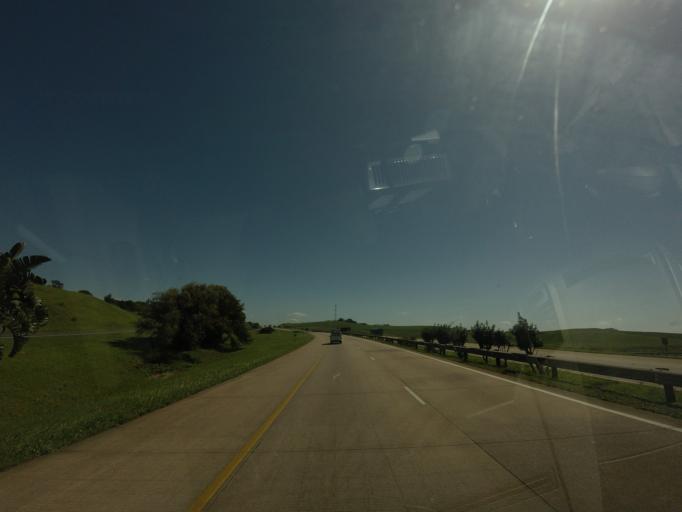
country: ZA
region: KwaZulu-Natal
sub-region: iLembe District Municipality
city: Stanger
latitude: -29.4307
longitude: 31.2723
